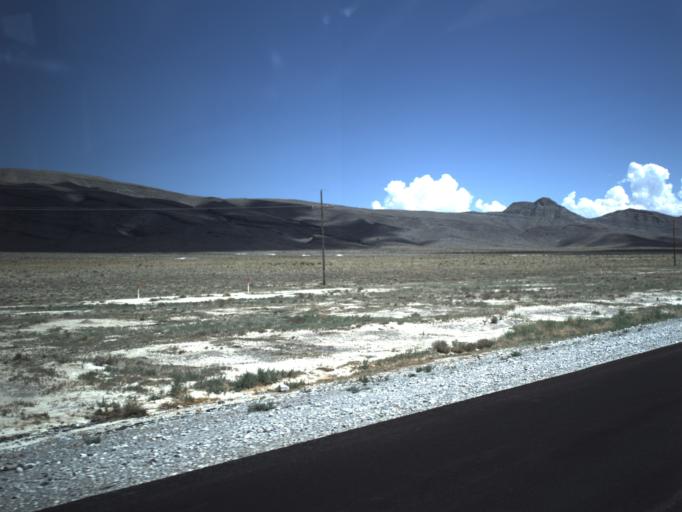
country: US
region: Utah
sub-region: Beaver County
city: Milford
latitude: 39.0545
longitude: -113.4269
